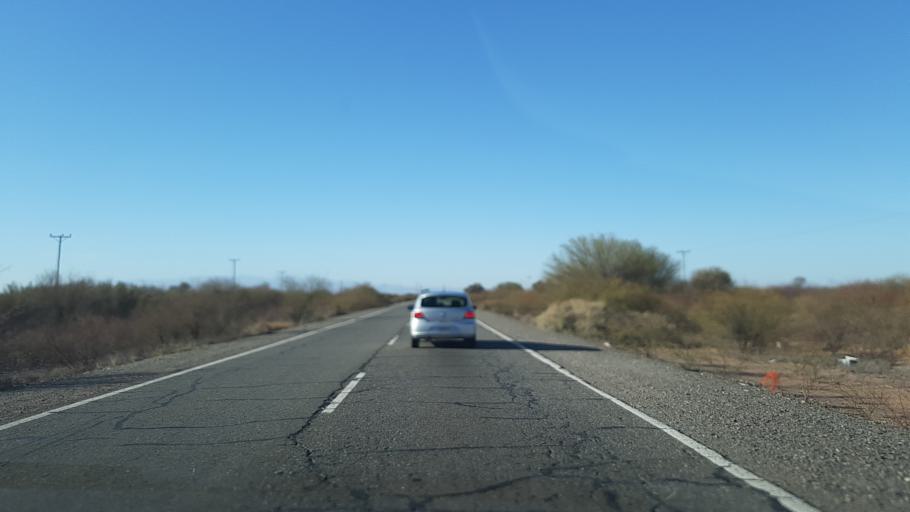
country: AR
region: San Juan
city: Caucete
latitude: -31.6134
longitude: -67.7246
